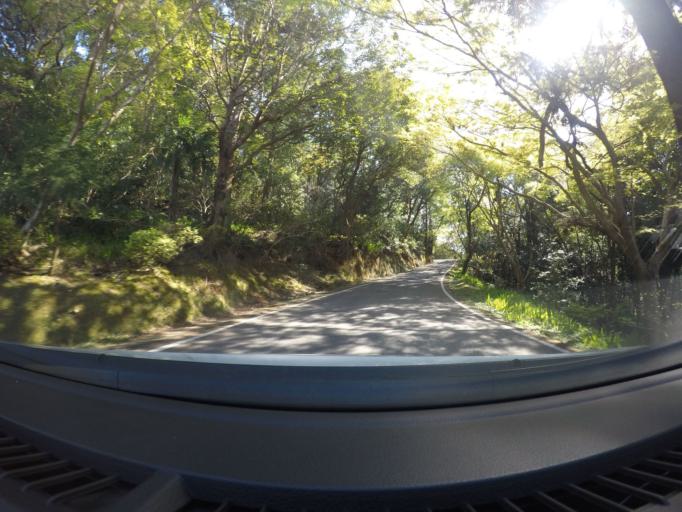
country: JP
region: Kochi
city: Kochi-shi
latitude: 33.5477
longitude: 133.5731
